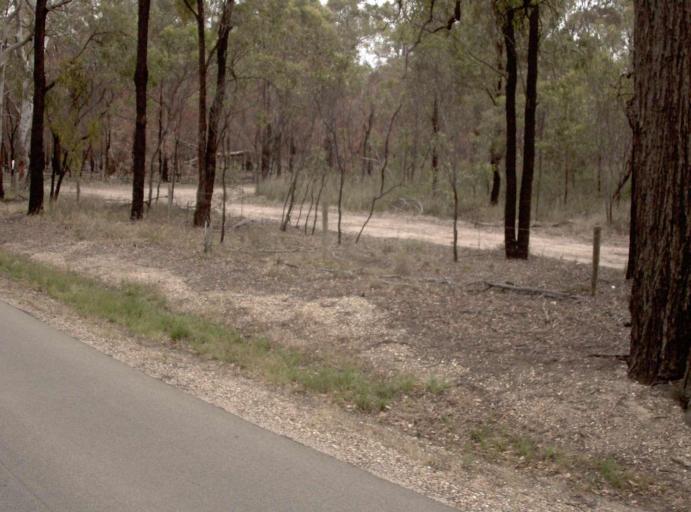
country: AU
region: Victoria
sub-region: Wellington
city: Heyfield
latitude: -37.9602
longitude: 146.7735
